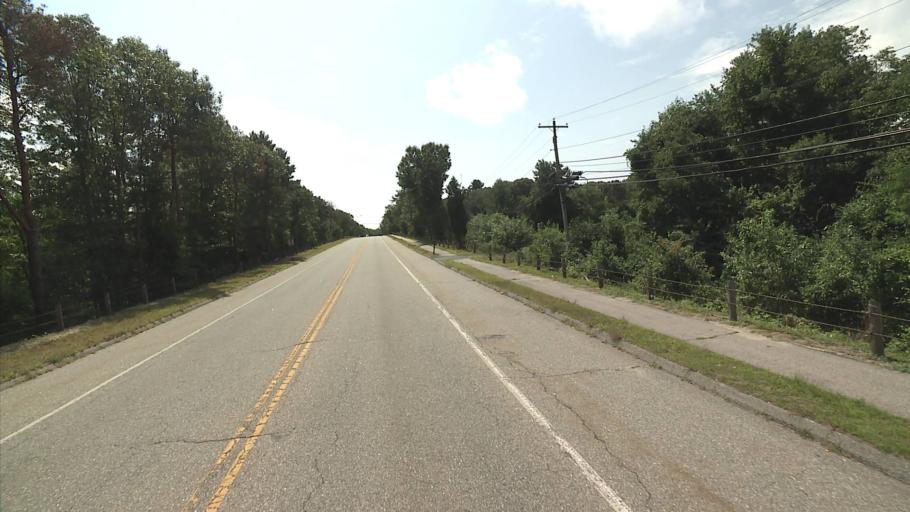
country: US
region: Connecticut
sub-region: New London County
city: Central Waterford
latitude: 41.3384
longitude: -72.1373
